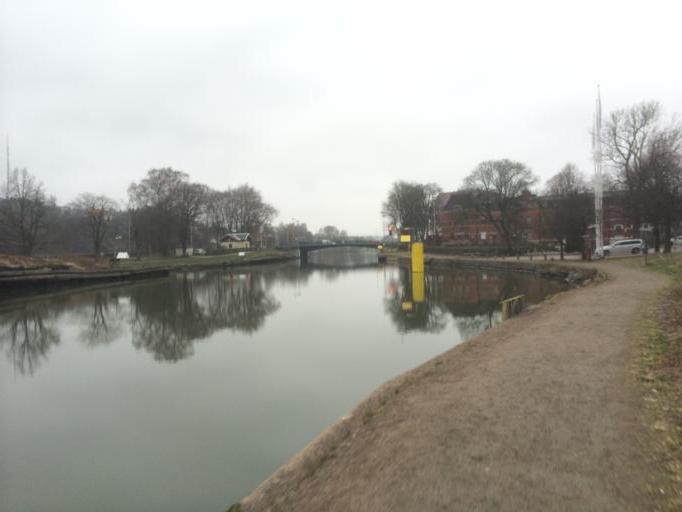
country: SE
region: Vaestra Goetaland
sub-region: Trollhattan
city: Trollhattan
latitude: 58.2818
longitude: 12.2838
